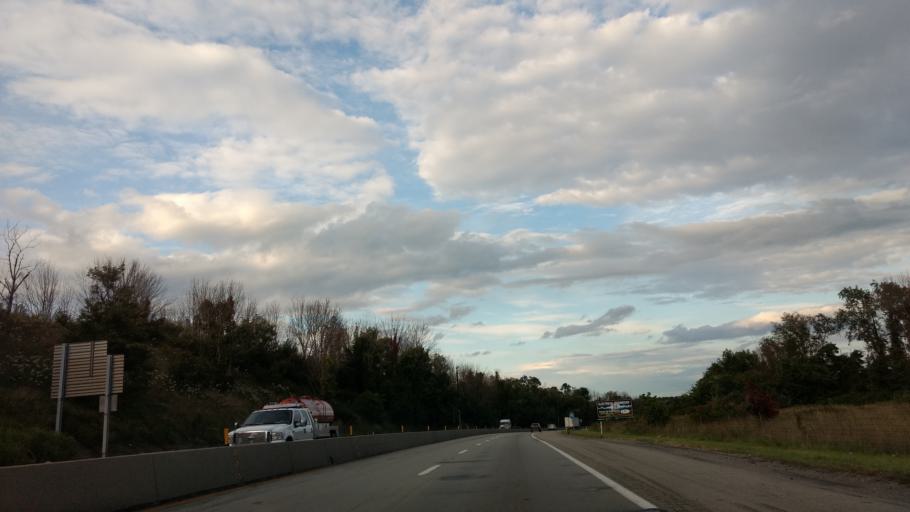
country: US
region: Pennsylvania
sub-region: Westmoreland County
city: Fellsburg
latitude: 40.1461
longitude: -79.8139
